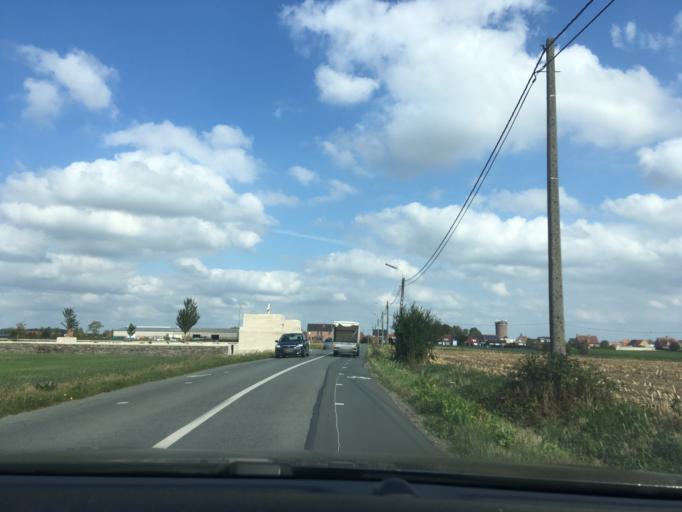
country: BE
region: Flanders
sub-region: Provincie West-Vlaanderen
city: Zonnebeke
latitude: 50.9039
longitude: 3.0100
